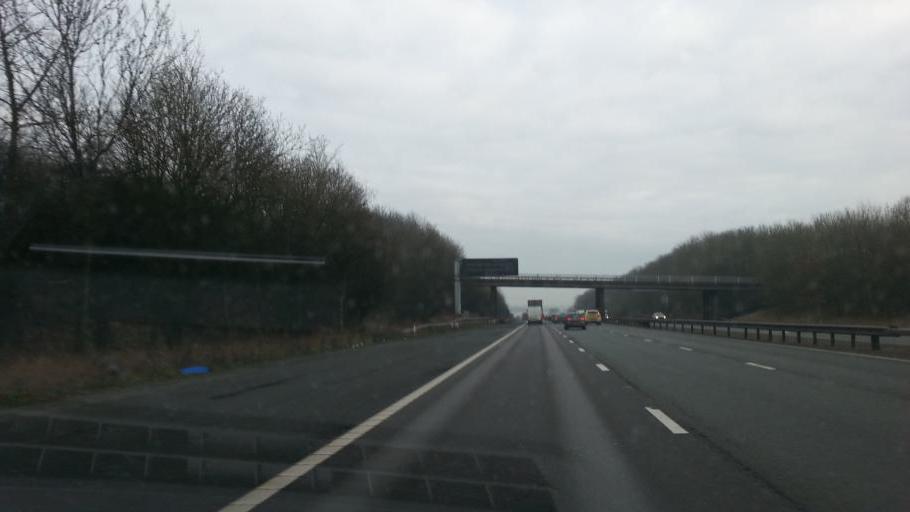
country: GB
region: England
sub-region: Warwickshire
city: Long Lawford
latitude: 52.4157
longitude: -1.2860
